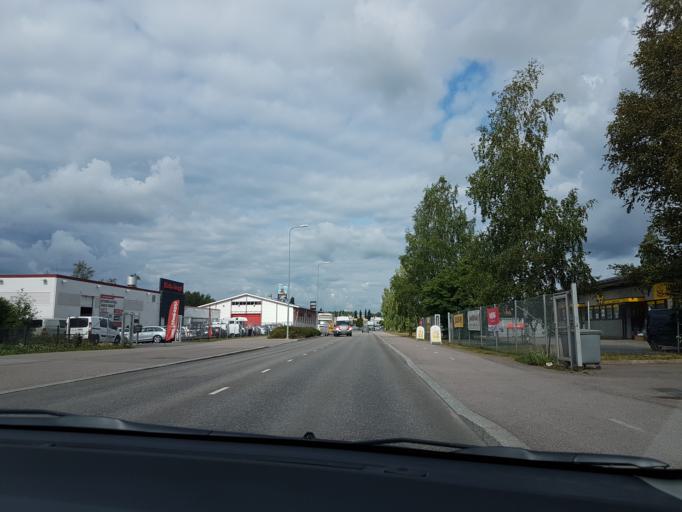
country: FI
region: Uusimaa
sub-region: Helsinki
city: Jaervenpaeae
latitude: 60.4729
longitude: 25.1149
